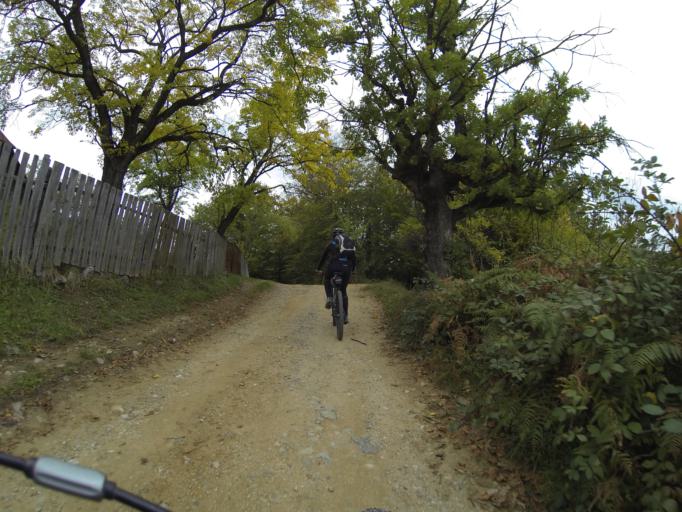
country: RO
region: Gorj
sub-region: Comuna Tismana
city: Sohodol
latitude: 45.0556
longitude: 22.8956
